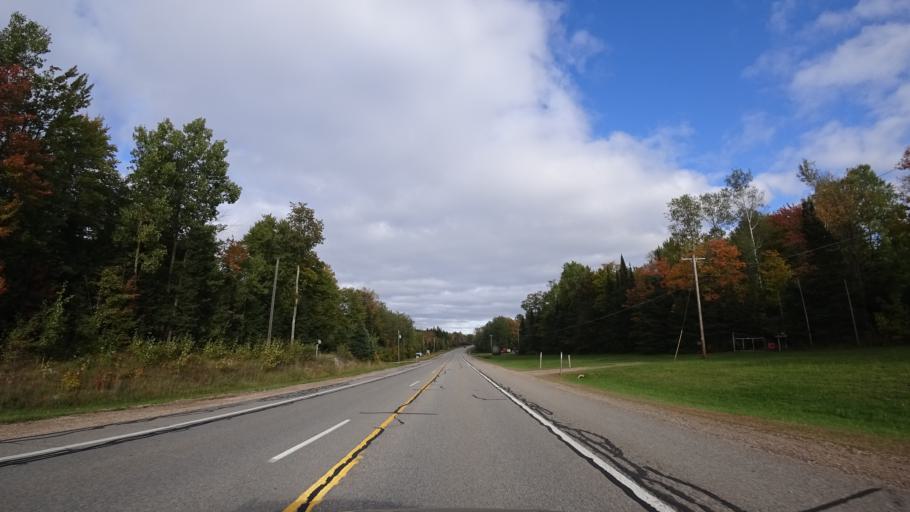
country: US
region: Michigan
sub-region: Alger County
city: Munising
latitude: 46.4417
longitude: -86.7455
